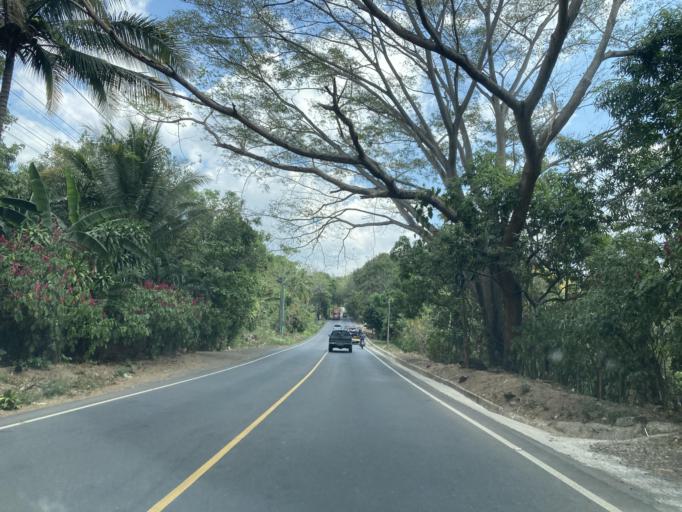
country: GT
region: Santa Rosa
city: Guazacapan
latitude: 14.0682
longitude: -90.4367
